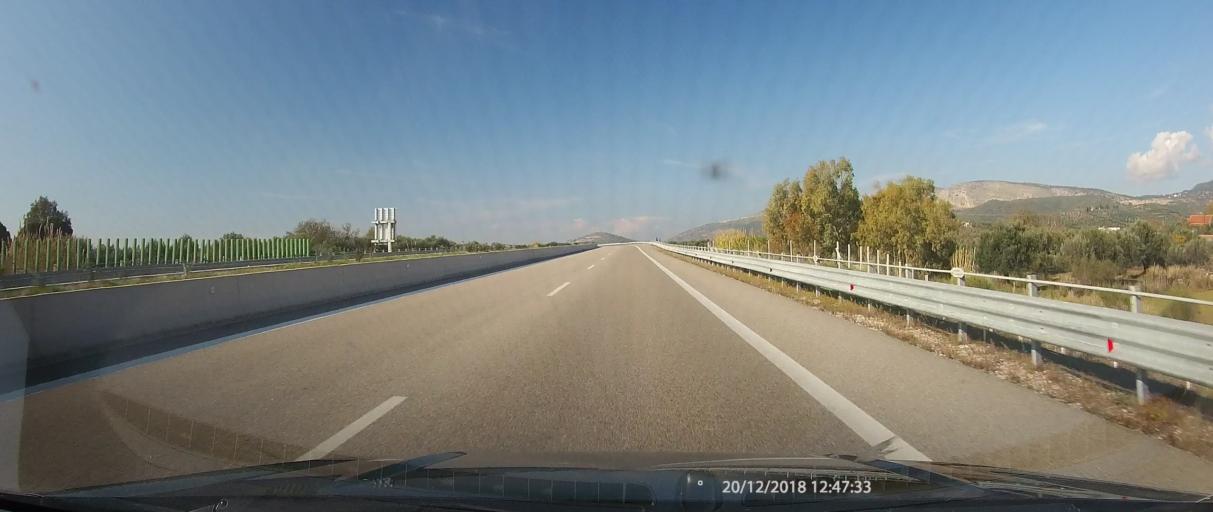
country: GR
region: West Greece
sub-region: Nomos Aitolias kai Akarnanias
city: Mesolongi
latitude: 38.3925
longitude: 21.4435
